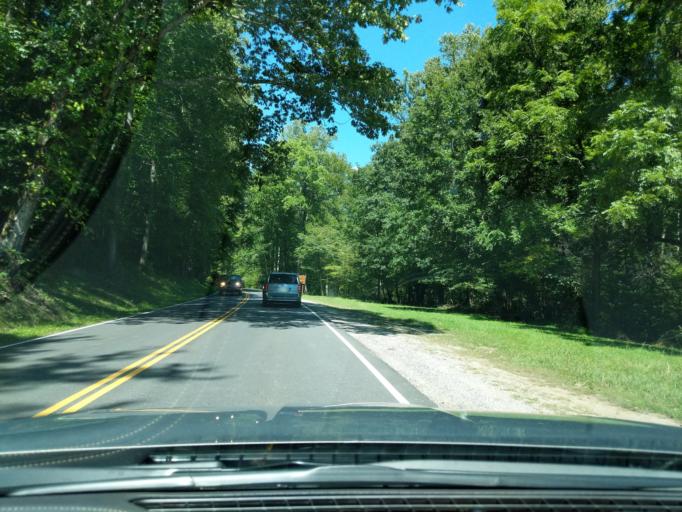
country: US
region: North Carolina
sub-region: Swain County
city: Cherokee
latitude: 35.5259
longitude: -83.3042
